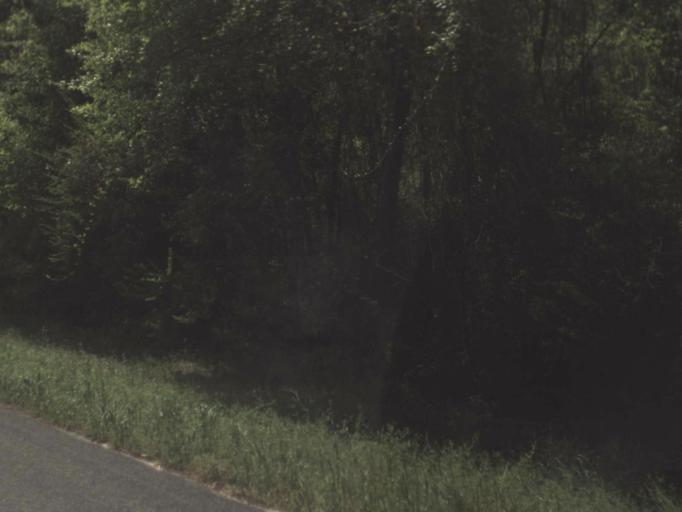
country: US
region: Florida
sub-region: Okaloosa County
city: Crestview
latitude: 30.9627
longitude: -86.6323
